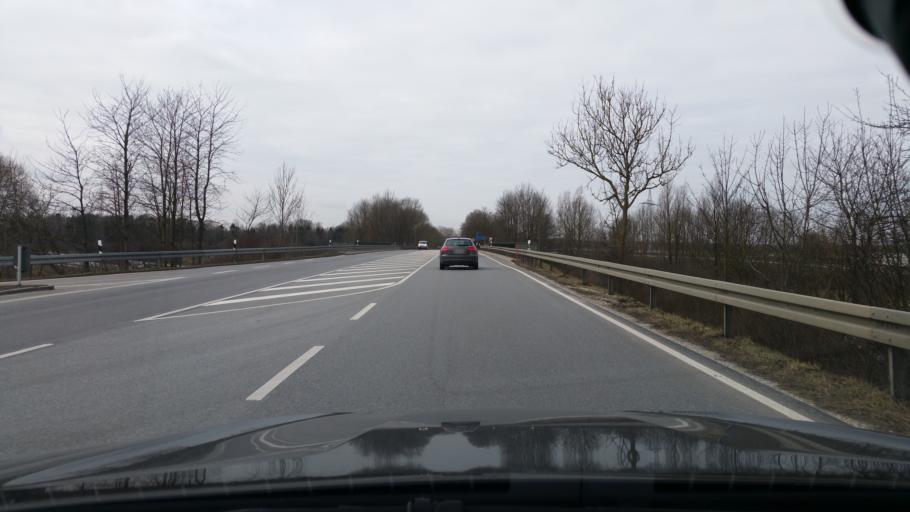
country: DE
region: Bavaria
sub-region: Upper Bavaria
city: Wang
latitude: 48.4811
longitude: 11.9933
